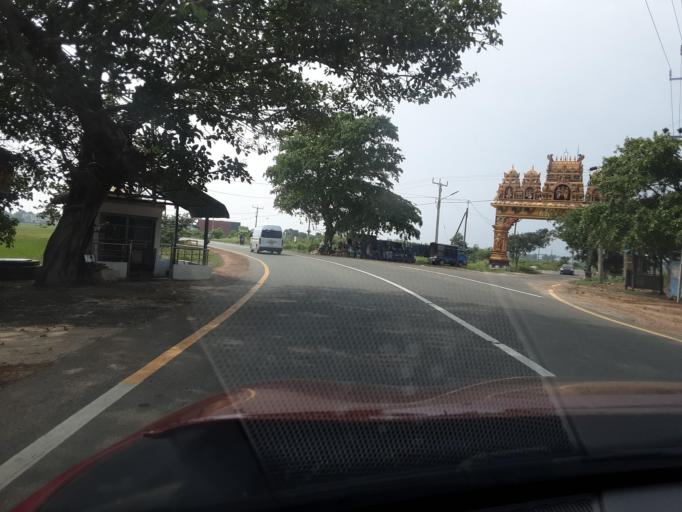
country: LK
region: Northern Province
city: Jaffna
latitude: 9.6628
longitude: 80.0627
